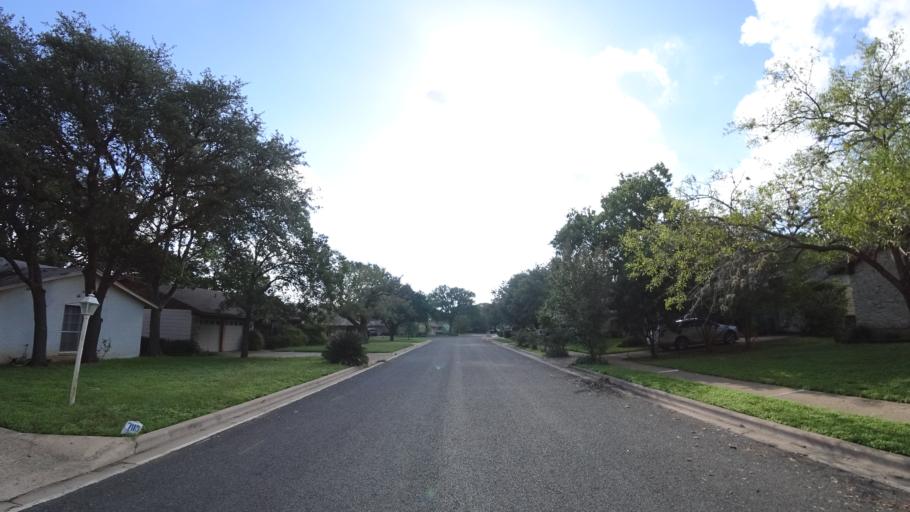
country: US
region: Texas
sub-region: Travis County
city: Rollingwood
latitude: 30.2154
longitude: -97.8020
